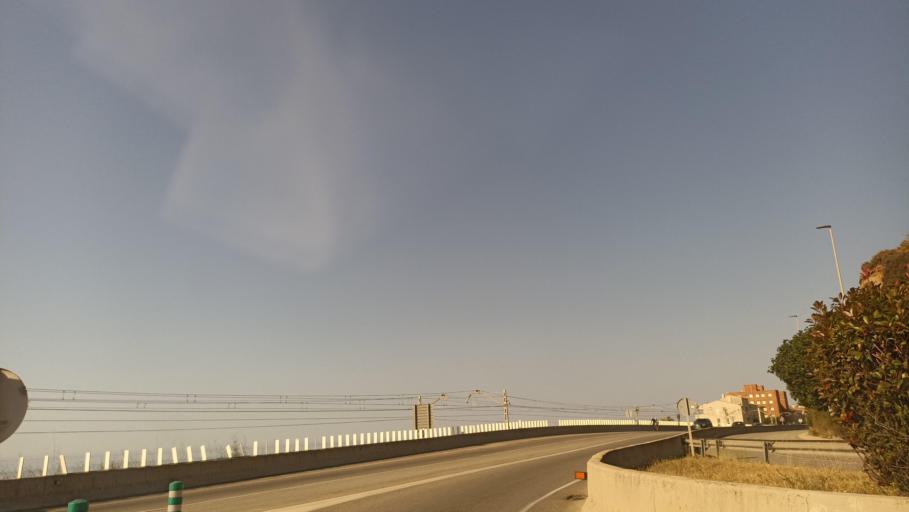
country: ES
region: Catalonia
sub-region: Provincia de Barcelona
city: Caldes d'Estrac
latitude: 41.5723
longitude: 2.5352
